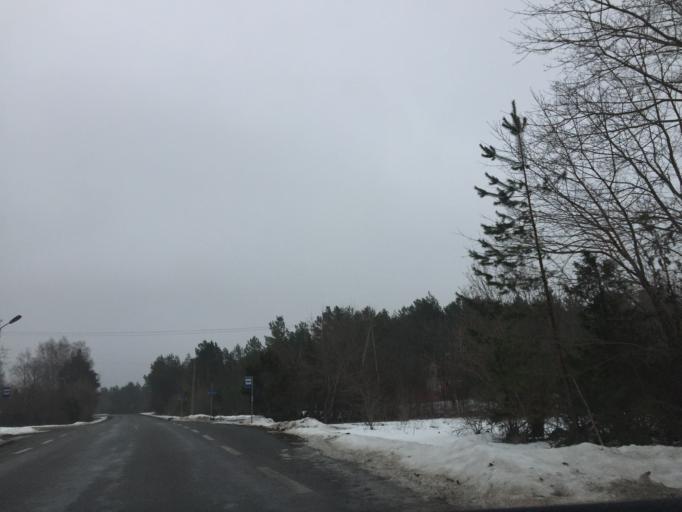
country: EE
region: Saare
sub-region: Orissaare vald
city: Orissaare
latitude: 58.4109
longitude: 22.8058
